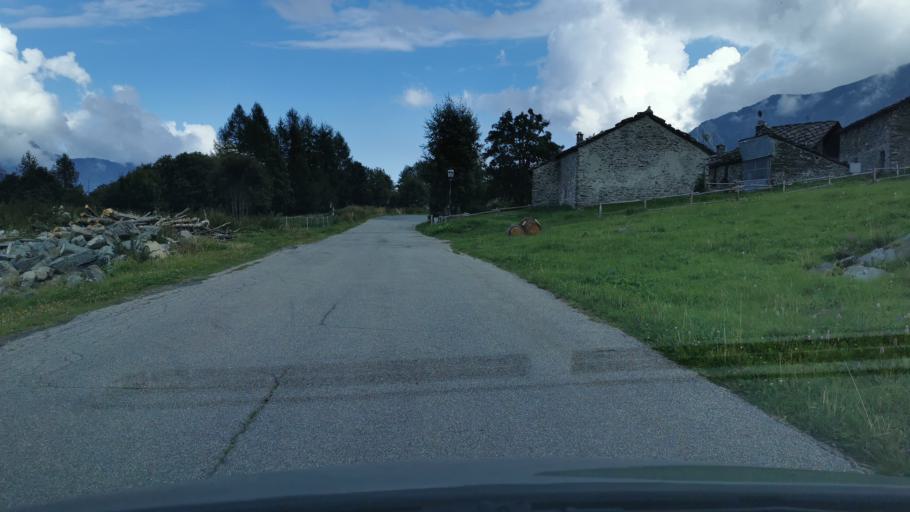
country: IT
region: Piedmont
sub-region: Provincia di Torino
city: Usseglio
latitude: 45.2226
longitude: 7.2300
